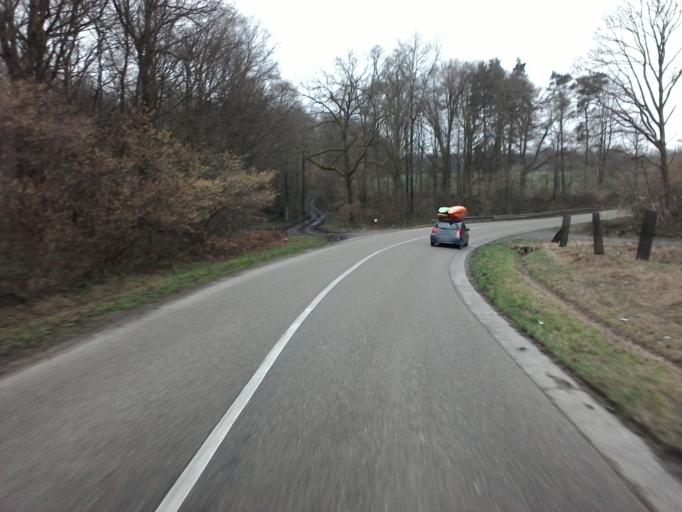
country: BE
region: Wallonia
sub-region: Province de Namur
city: Gedinne
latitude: 50.0397
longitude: 4.9626
